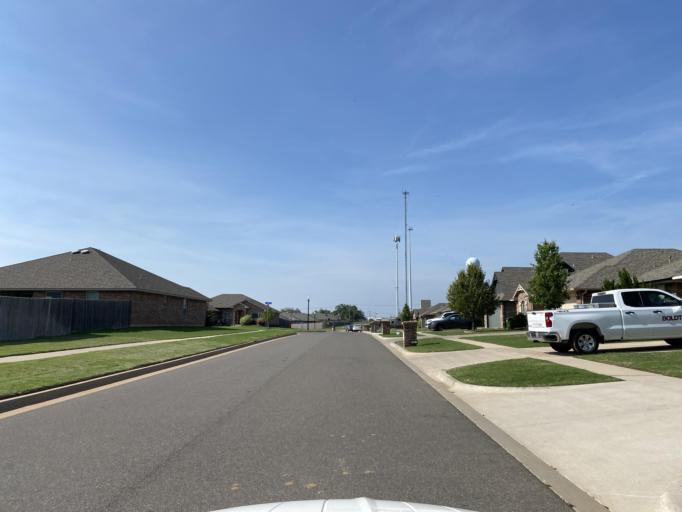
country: US
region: Oklahoma
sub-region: Oklahoma County
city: Nicoma Park
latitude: 35.4401
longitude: -97.3410
